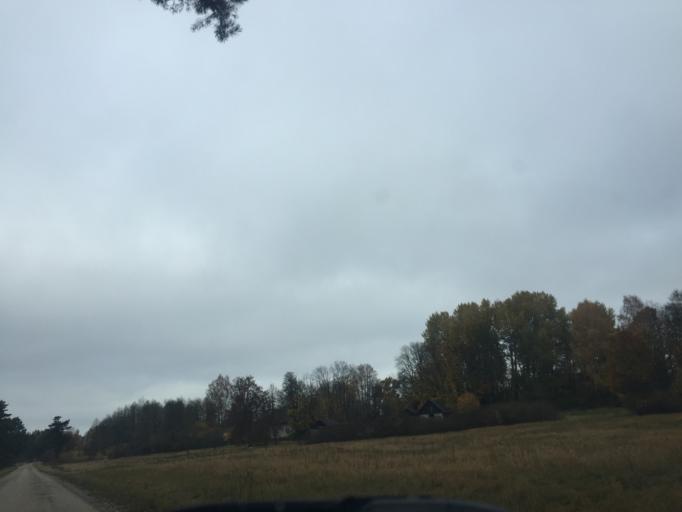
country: LV
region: Jaunpils
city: Jaunpils
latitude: 56.6902
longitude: 23.1165
